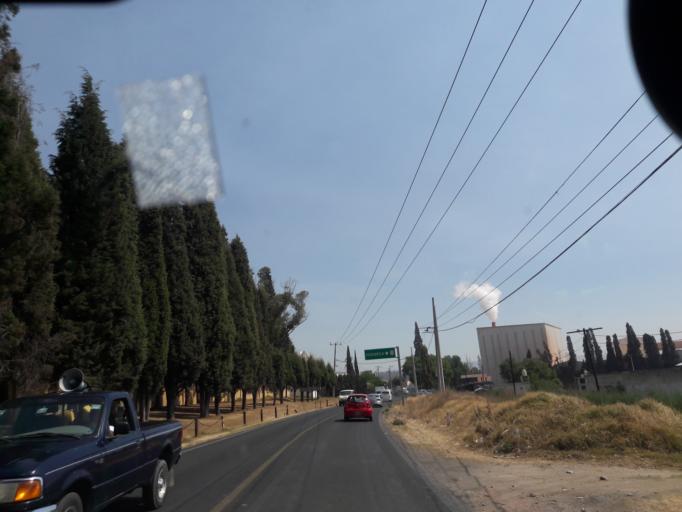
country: MX
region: Tlaxcala
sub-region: Ixtacuixtla de Mariano Matamoros
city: Villa Mariano Matamoros
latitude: 19.3034
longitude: -98.3979
